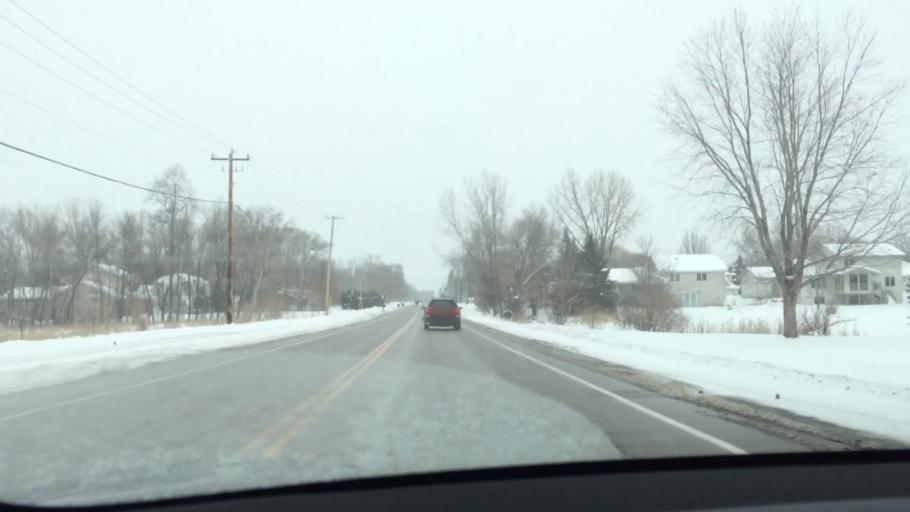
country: US
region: Minnesota
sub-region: Anoka County
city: Circle Pines
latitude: 45.1159
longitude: -93.1274
